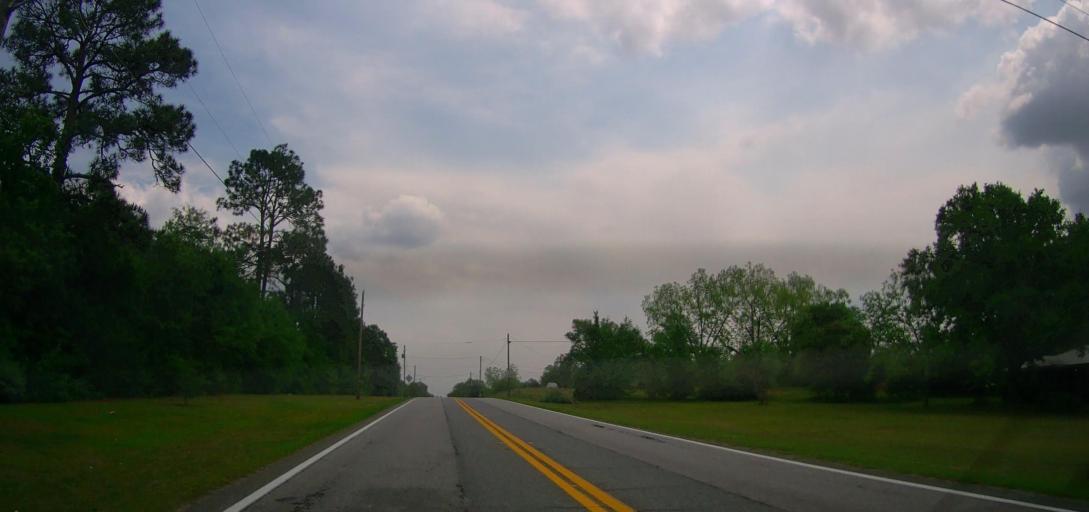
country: US
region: Georgia
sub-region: Treutlen County
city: Soperton
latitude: 32.3839
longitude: -82.6010
